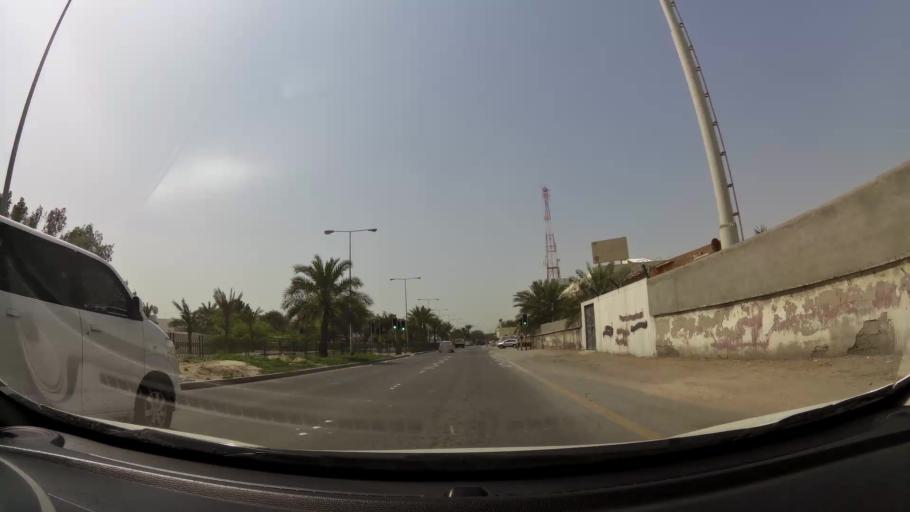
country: BH
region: Manama
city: Jidd Hafs
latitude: 26.2151
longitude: 50.4653
